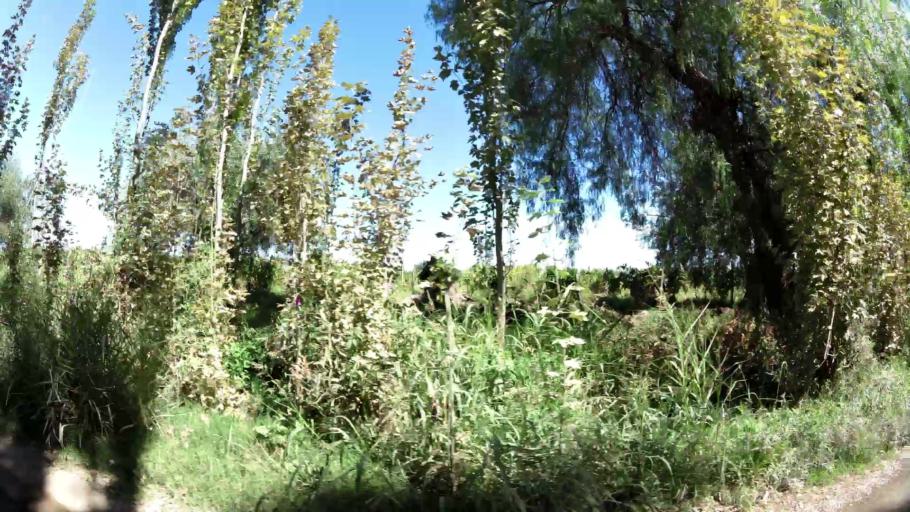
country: AR
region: Mendoza
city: Lujan de Cuyo
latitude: -32.9906
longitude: -68.8551
